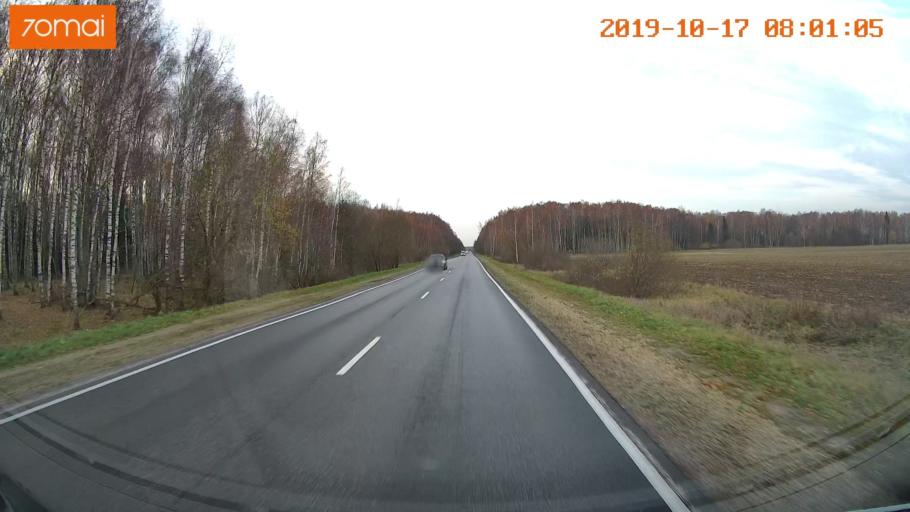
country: RU
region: Vladimir
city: Bavleny
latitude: 56.3767
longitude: 39.5042
